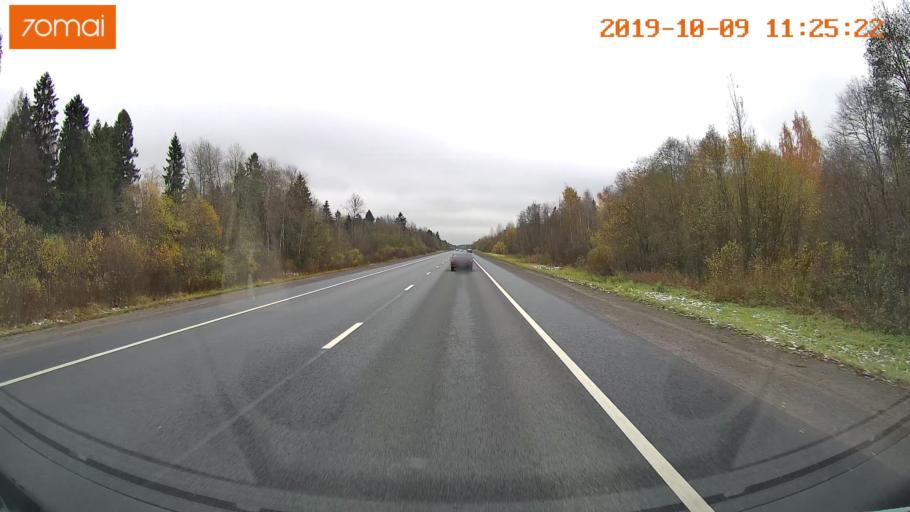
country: RU
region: Vologda
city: Vologda
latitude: 59.1015
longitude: 39.9909
